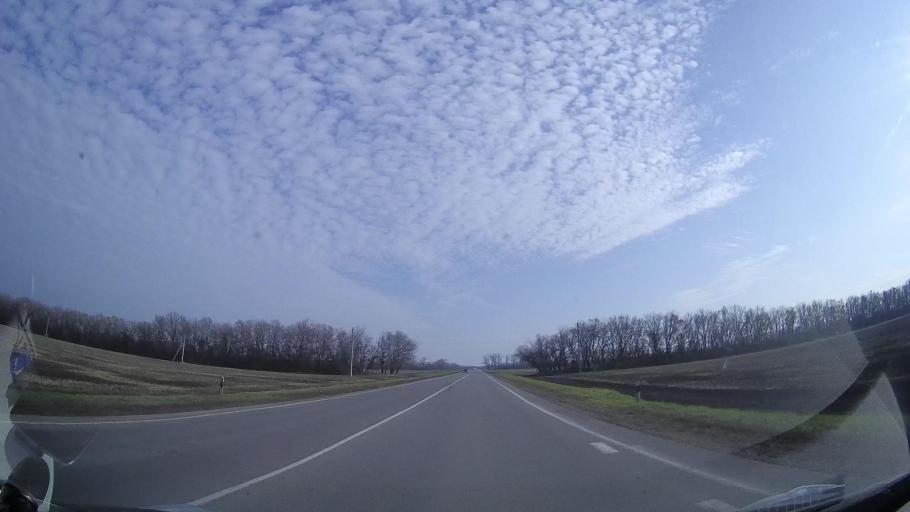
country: RU
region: Rostov
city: Tselina
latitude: 46.5230
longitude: 41.1273
